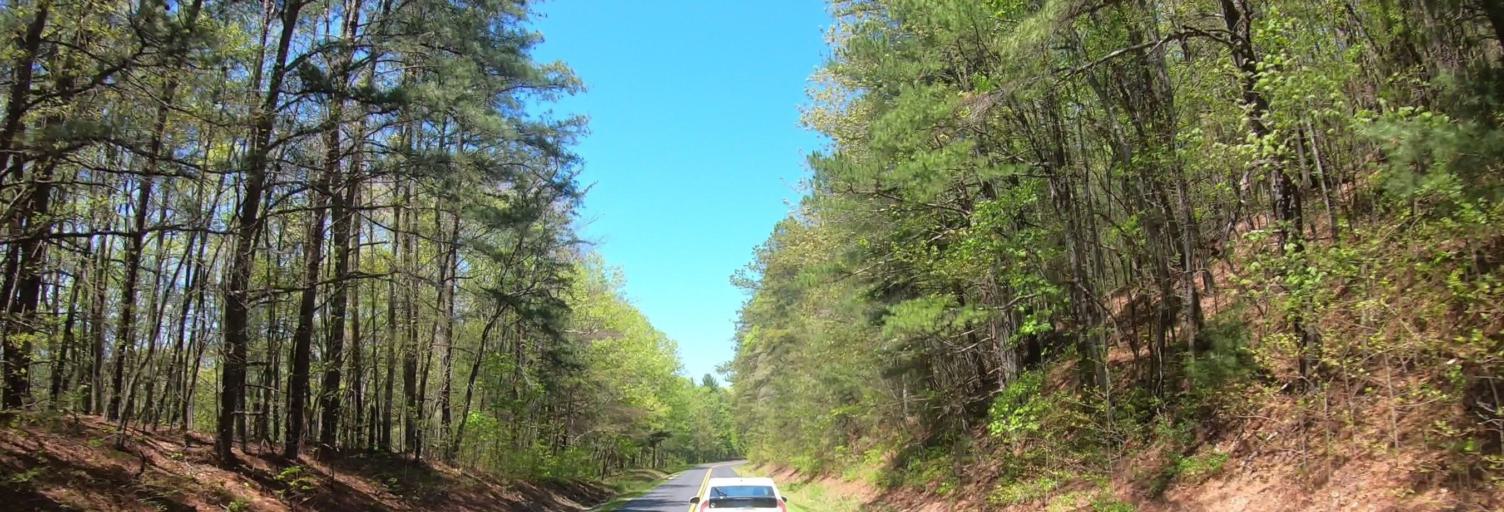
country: US
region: North Carolina
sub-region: Buncombe County
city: Biltmore Forest
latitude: 35.5428
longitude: -82.4987
